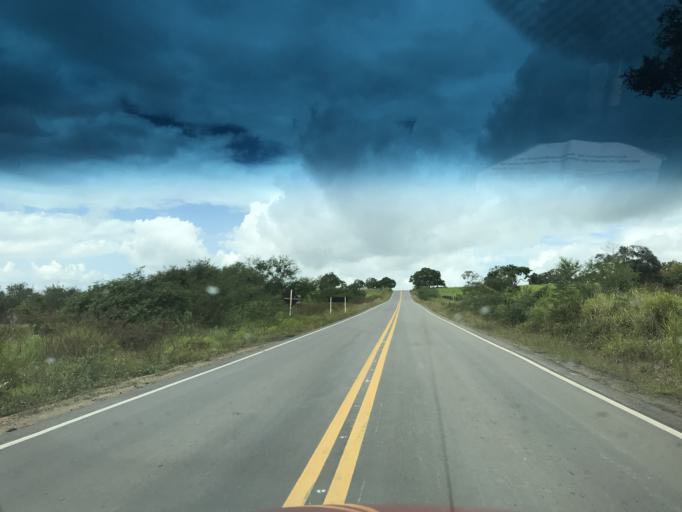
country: BR
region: Bahia
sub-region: Conceicao Do Almeida
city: Conceicao do Almeida
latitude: -12.6824
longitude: -39.2547
